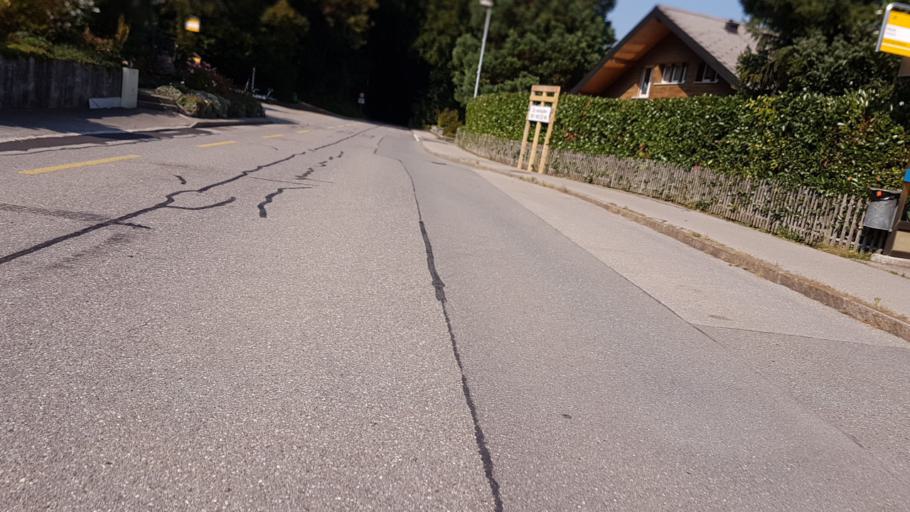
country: CH
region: Bern
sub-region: Frutigen-Niedersimmental District
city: Spiez
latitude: 46.6752
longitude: 7.6850
